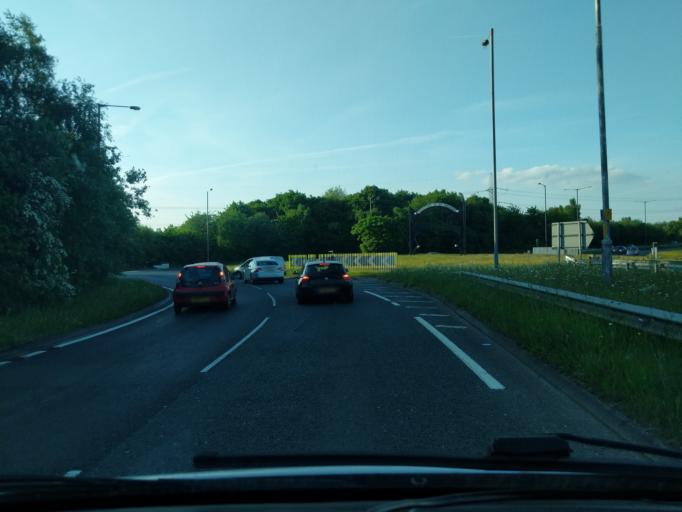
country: GB
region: England
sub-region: St. Helens
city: St Helens
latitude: 53.4181
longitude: -2.7456
